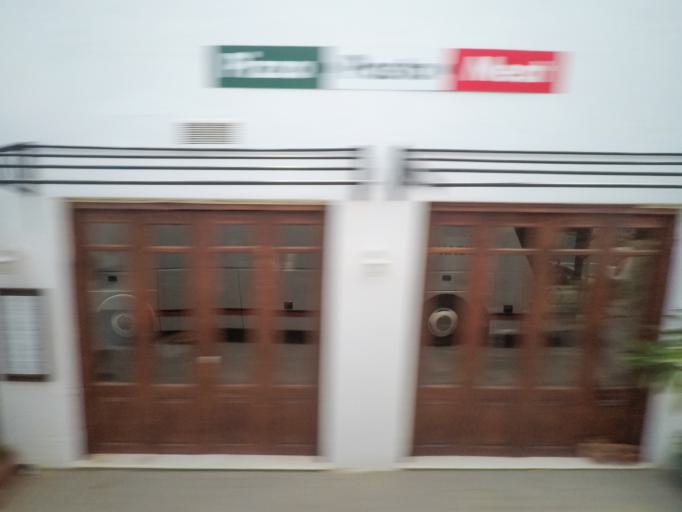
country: GR
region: Crete
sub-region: Nomos Lasithiou
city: Agios Nikolaos
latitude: 35.1901
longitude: 25.7222
